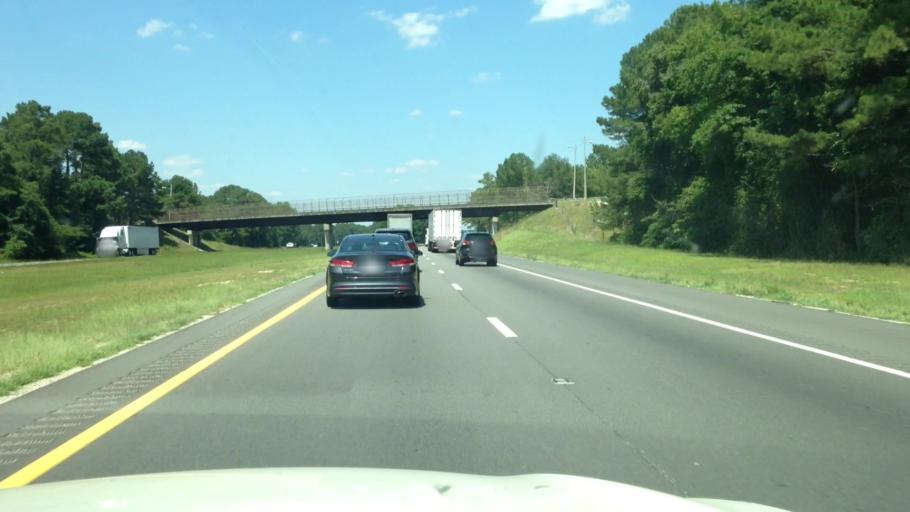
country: US
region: North Carolina
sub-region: Cumberland County
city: Vander
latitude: 34.9883
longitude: -78.8388
